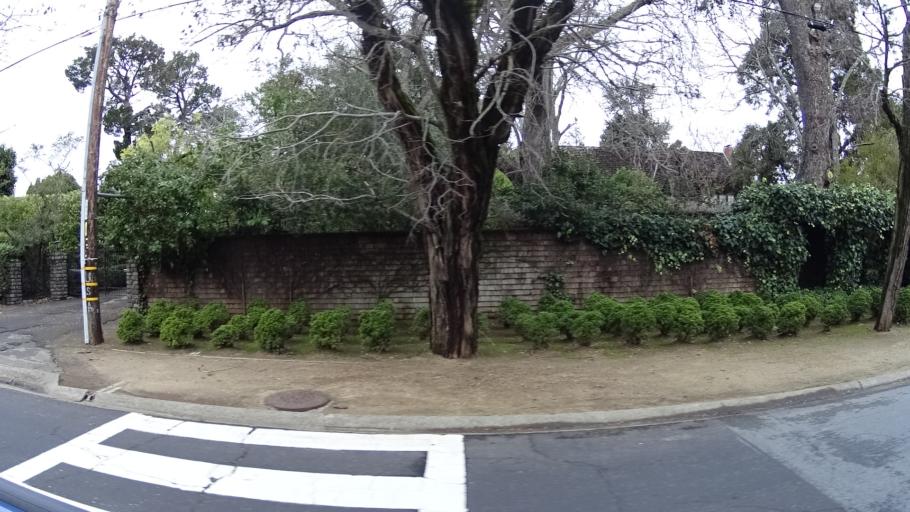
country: US
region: California
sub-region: San Mateo County
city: San Mateo
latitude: 37.5671
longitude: -122.3371
